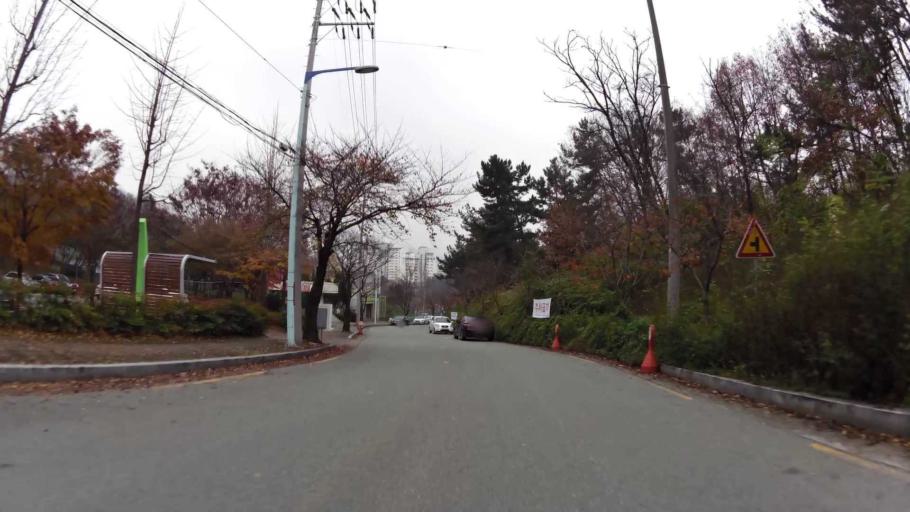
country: KR
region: Daegu
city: Daegu
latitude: 35.8560
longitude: 128.6586
